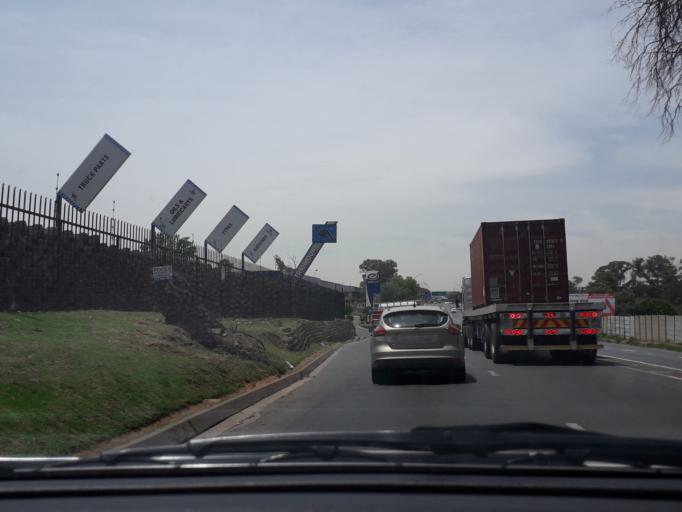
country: ZA
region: Gauteng
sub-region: City of Johannesburg Metropolitan Municipality
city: Roodepoort
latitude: -26.1841
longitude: 27.9410
